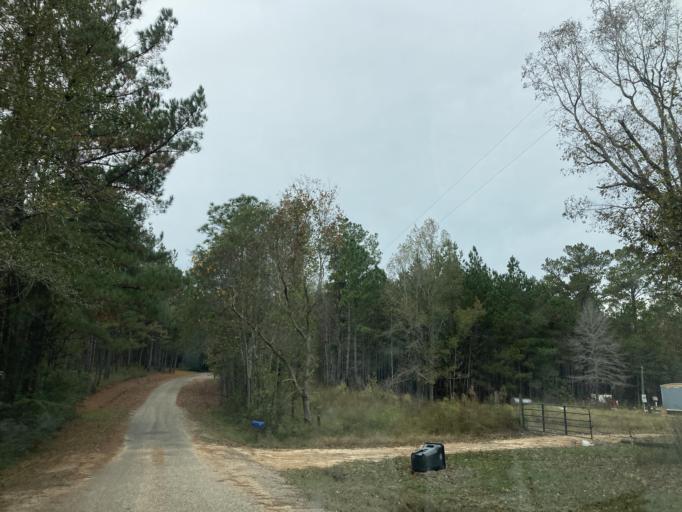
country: US
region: Mississippi
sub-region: Lamar County
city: Lumberton
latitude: 31.0540
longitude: -89.5133
